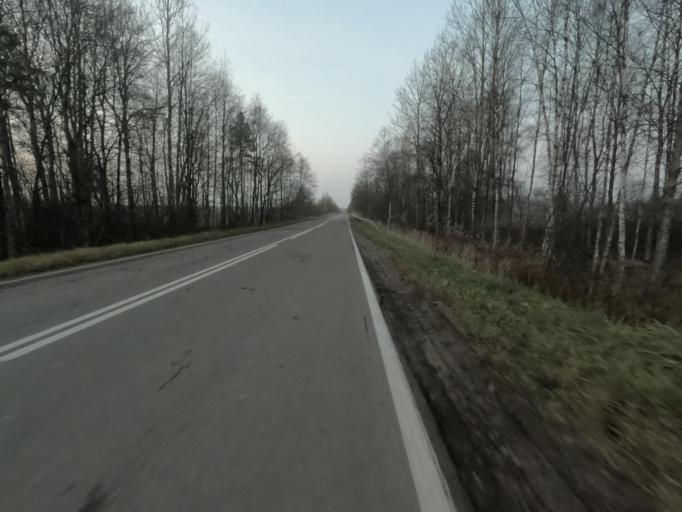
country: RU
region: Leningrad
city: Kirovsk
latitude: 59.8589
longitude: 30.9813
